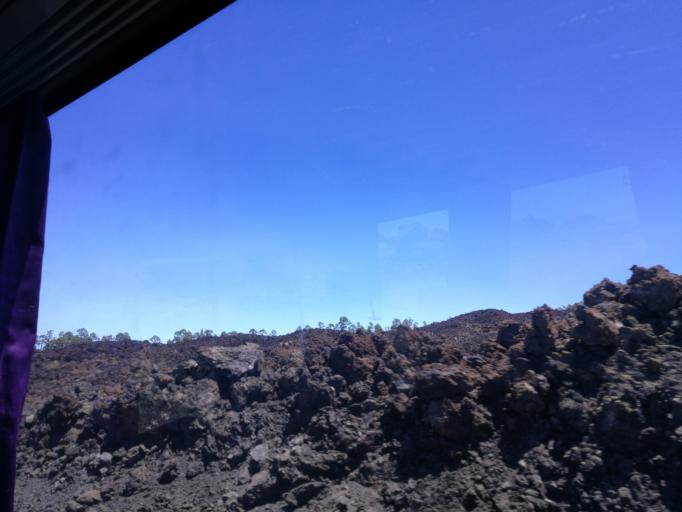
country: ES
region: Canary Islands
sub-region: Provincia de Santa Cruz de Tenerife
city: Guia de Isora
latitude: 28.2745
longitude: -16.7287
